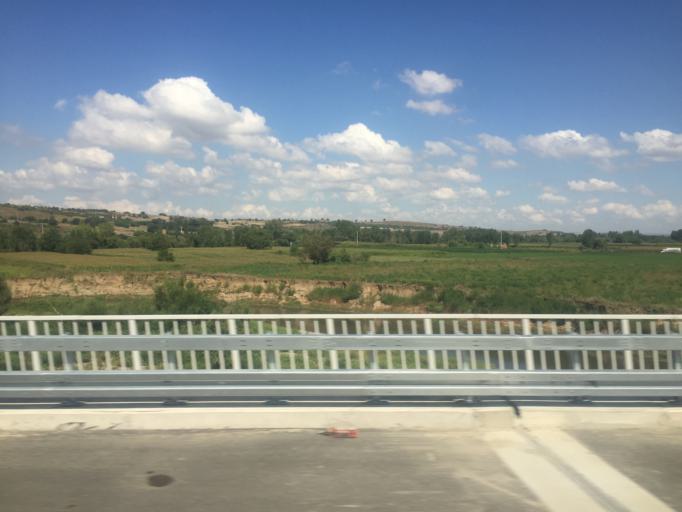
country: TR
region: Balikesir
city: Gobel
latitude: 39.9824
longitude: 28.1793
